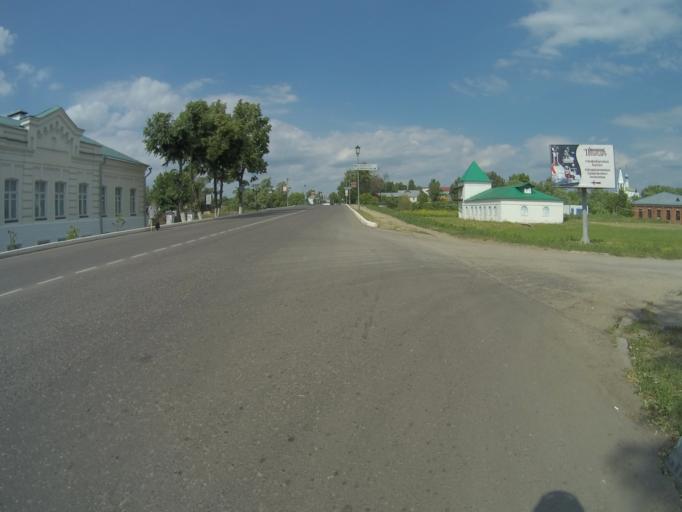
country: RU
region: Vladimir
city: Suzdal'
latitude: 56.4130
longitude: 40.4476
